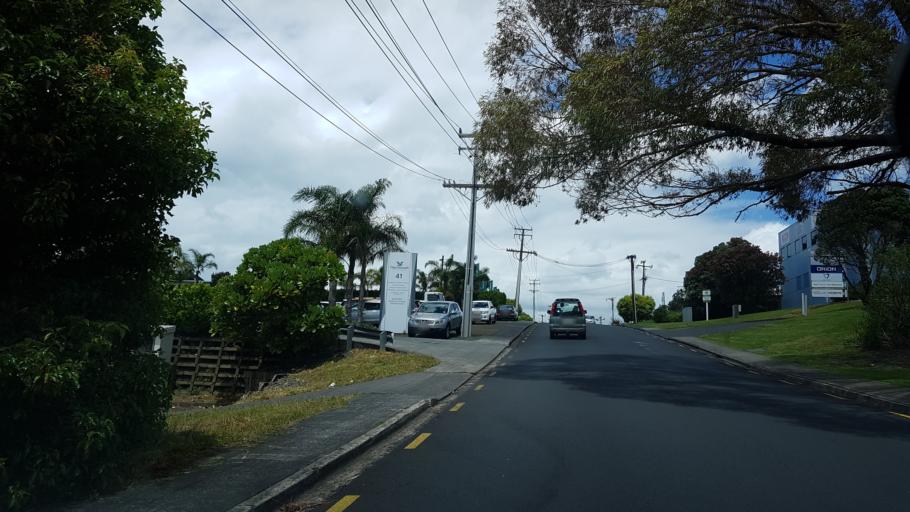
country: NZ
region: Auckland
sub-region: Auckland
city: North Shore
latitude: -36.7750
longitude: 174.7387
